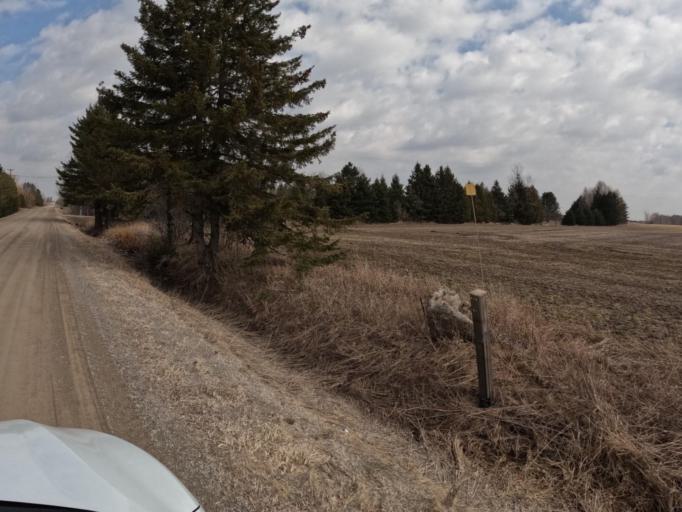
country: CA
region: Ontario
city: Orangeville
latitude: 43.9015
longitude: -80.2355
